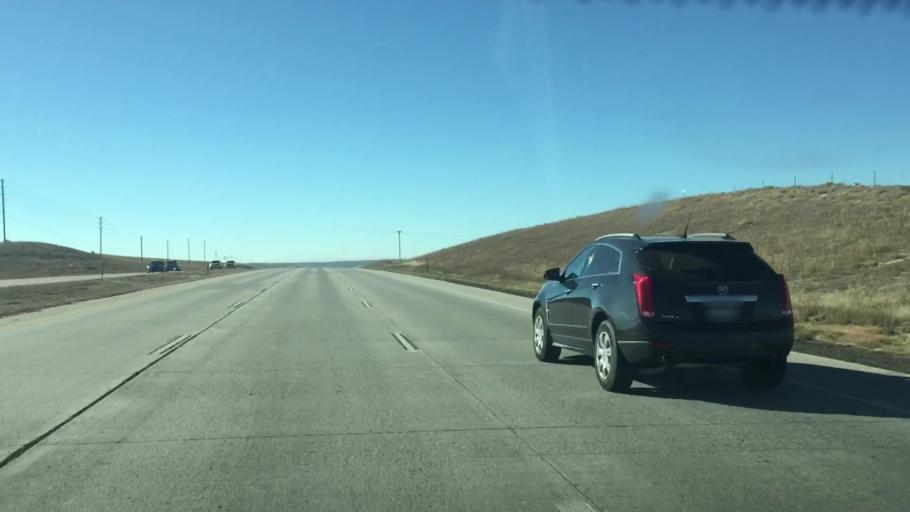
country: US
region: Colorado
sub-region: Douglas County
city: The Pinery
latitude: 39.4697
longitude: -104.7587
